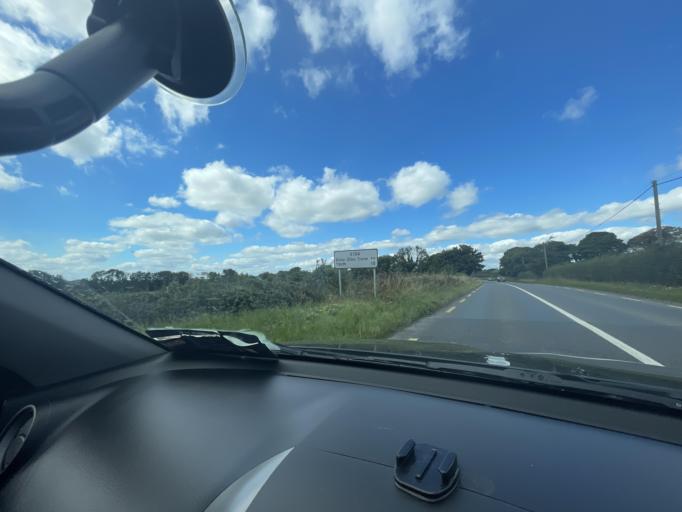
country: IE
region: Leinster
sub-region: An Mhi
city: Dunshaughlin
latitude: 53.5033
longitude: -6.5989
